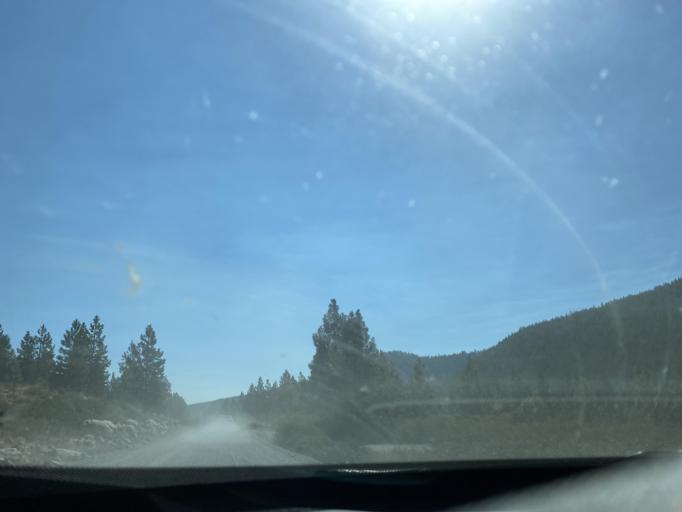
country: US
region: Oregon
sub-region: Deschutes County
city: Sunriver
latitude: 44.0346
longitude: -121.5366
